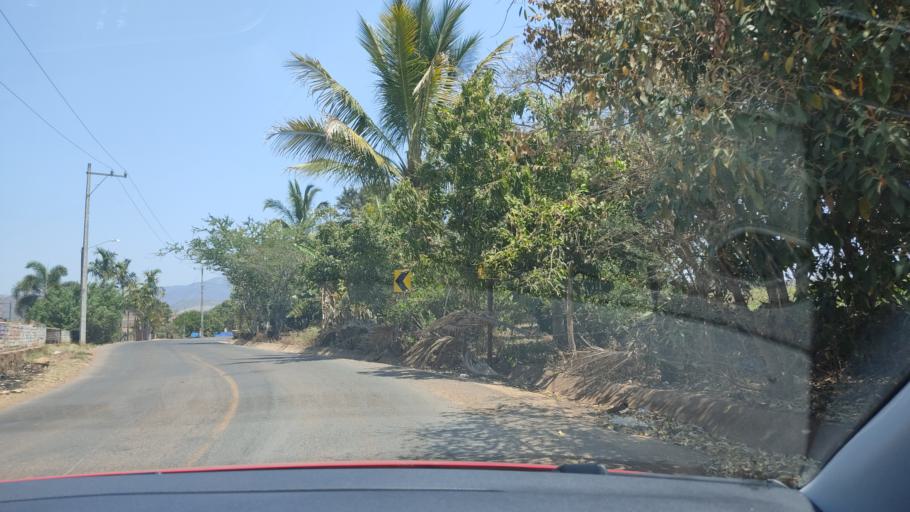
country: MX
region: Nayarit
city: Puga
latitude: 21.5763
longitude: -104.7831
